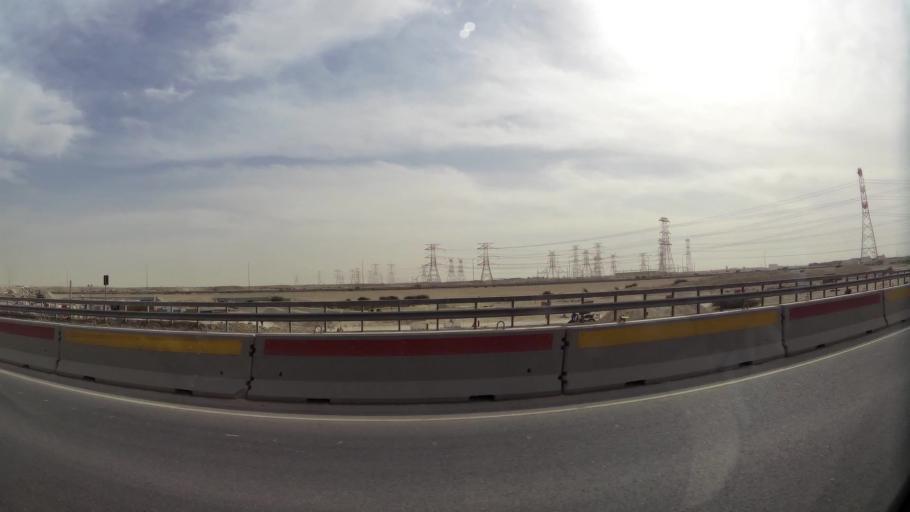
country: QA
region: Baladiyat ar Rayyan
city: Ash Shahaniyah
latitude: 25.3405
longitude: 51.3174
